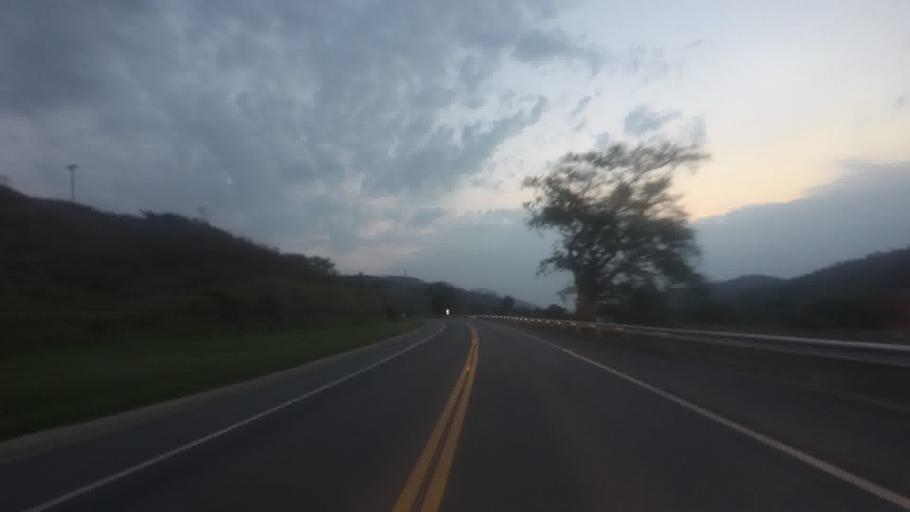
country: BR
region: Minas Gerais
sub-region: Alem Paraiba
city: Alem Paraiba
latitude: -21.9051
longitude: -42.7316
